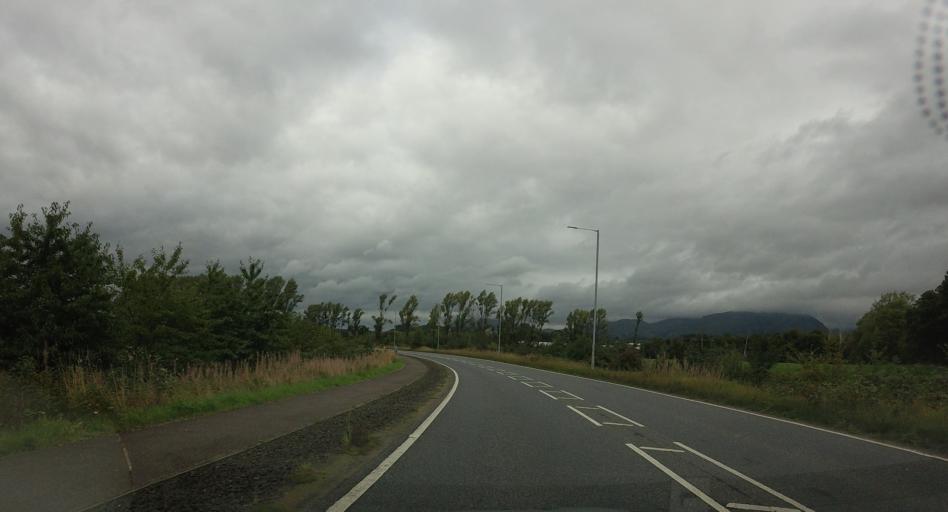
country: GB
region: Scotland
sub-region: Clackmannanshire
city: Alloa
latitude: 56.1170
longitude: -3.7702
